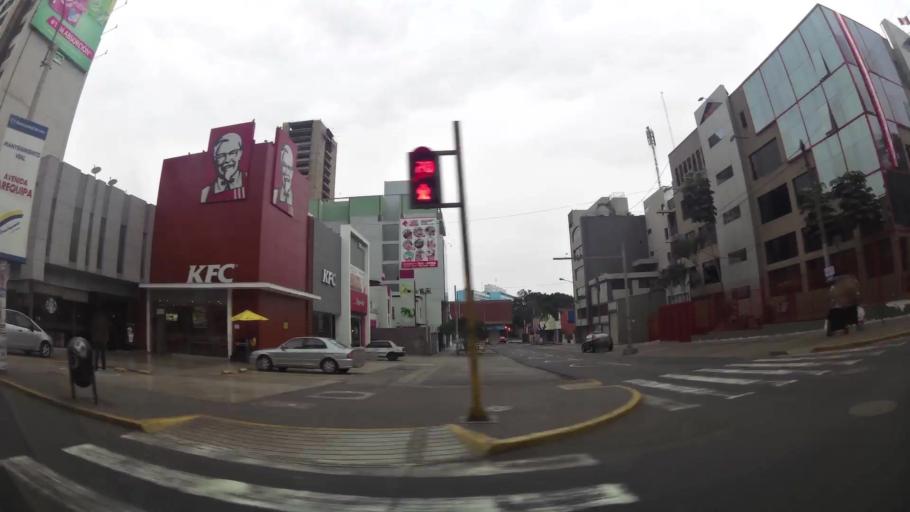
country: PE
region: Lima
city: Lima
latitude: -12.0778
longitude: -77.0356
